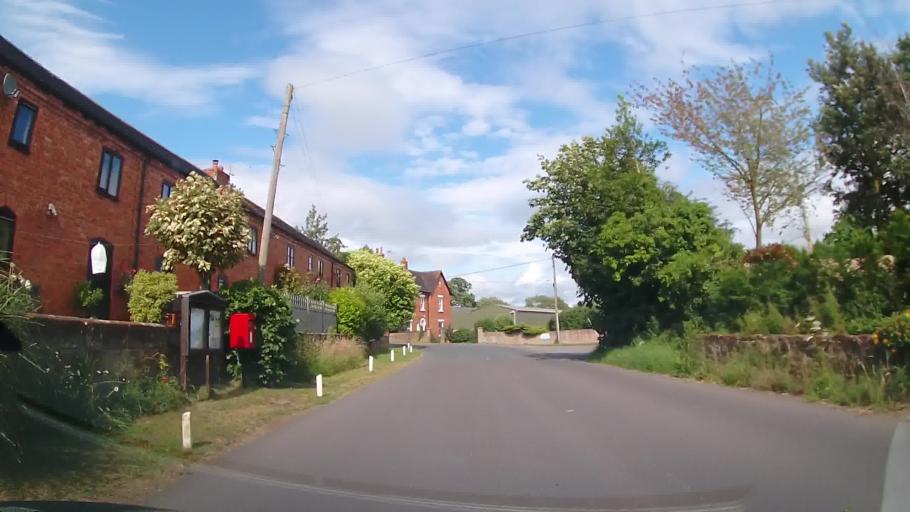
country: GB
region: England
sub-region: Shropshire
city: Petton
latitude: 52.8290
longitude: -2.8058
